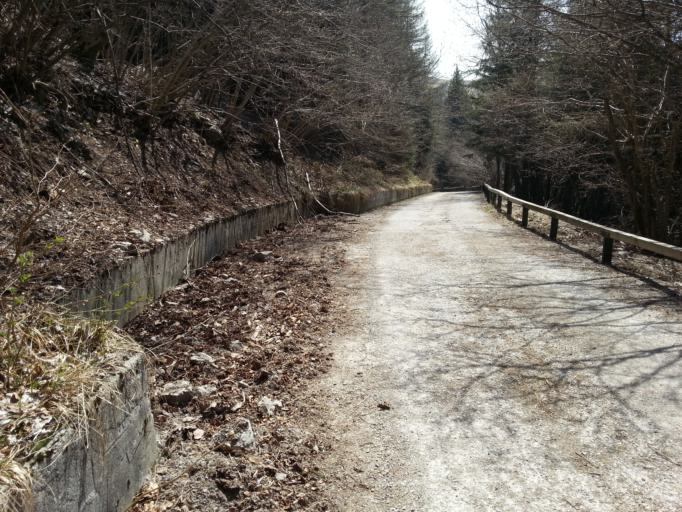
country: IT
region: Lombardy
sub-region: Provincia di Lecco
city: Suello
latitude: 45.8466
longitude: 9.3175
